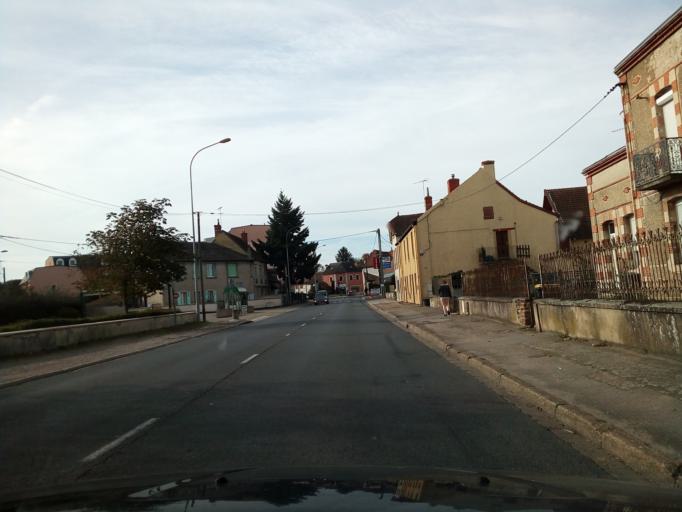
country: FR
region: Auvergne
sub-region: Departement de l'Allier
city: Saint-Pourcain-sur-Sioule
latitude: 46.3065
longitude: 3.2990
